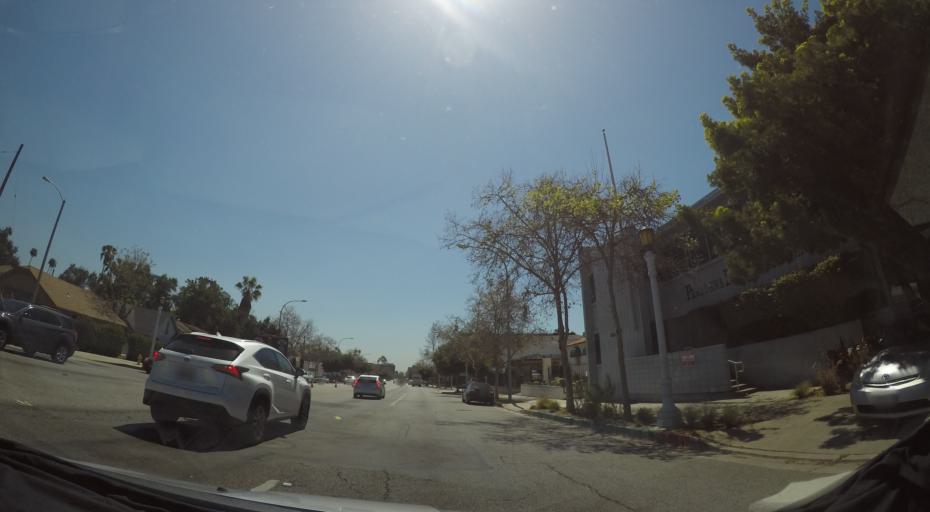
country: US
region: California
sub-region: Los Angeles County
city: Pasadena
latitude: 34.1636
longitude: -118.1326
